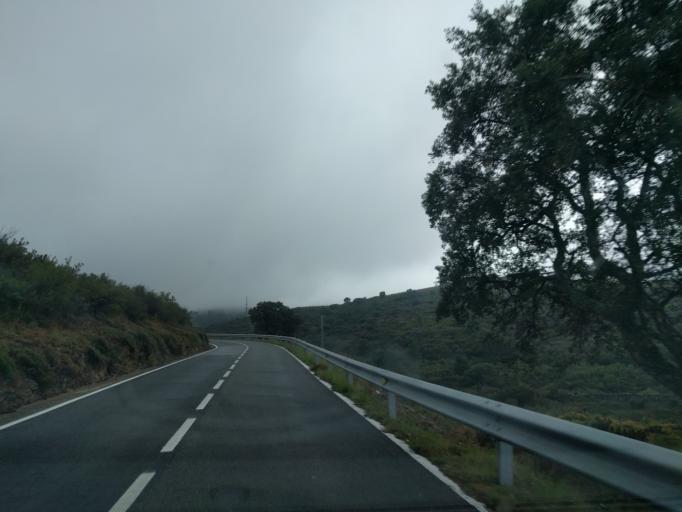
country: ES
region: Catalonia
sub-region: Provincia de Girona
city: Cadaques
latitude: 42.3004
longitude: 3.2299
